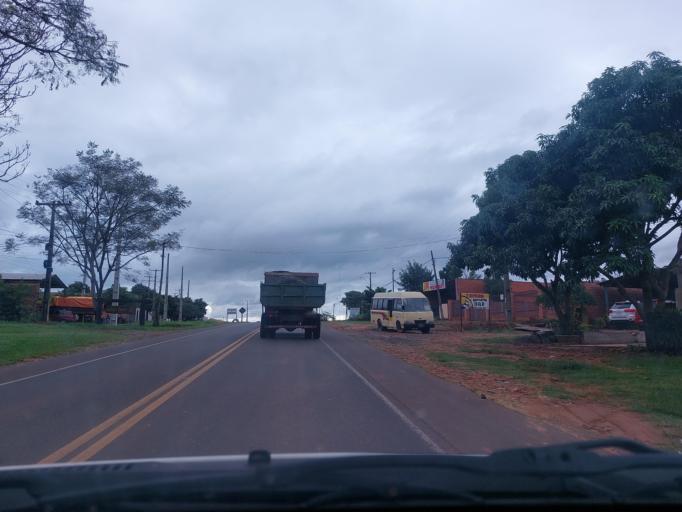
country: PY
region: San Pedro
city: Guayaybi
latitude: -24.6635
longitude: -56.4188
